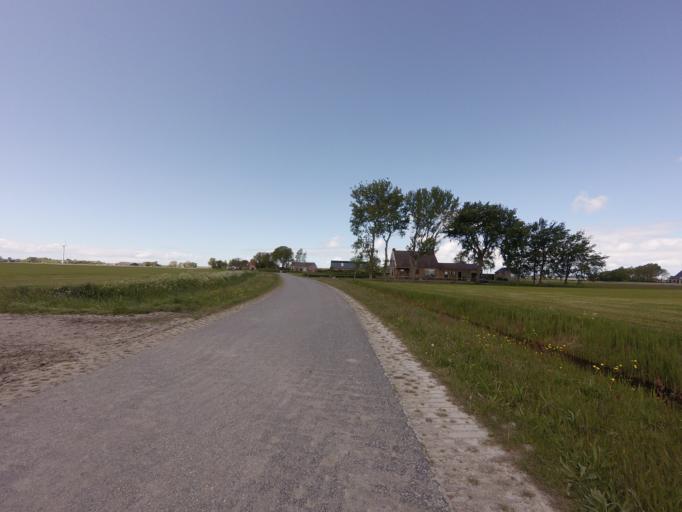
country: NL
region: Friesland
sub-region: Gemeente Harlingen
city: Harlingen
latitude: 53.1193
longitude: 5.4334
